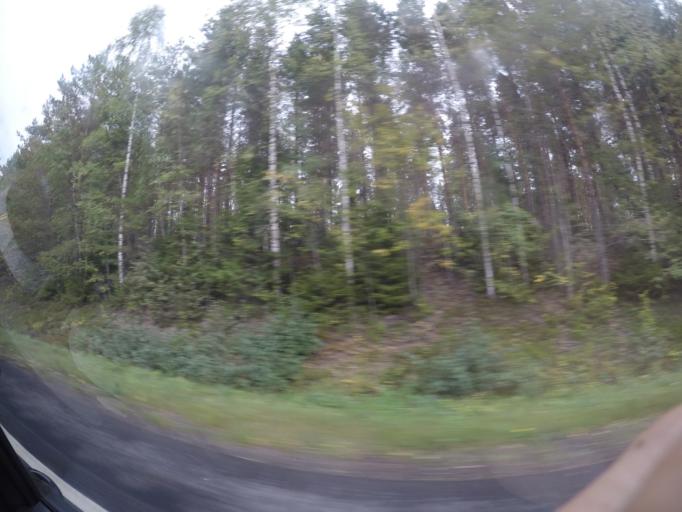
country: FI
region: Haeme
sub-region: Haemeenlinna
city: Parola
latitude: 61.1323
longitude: 24.4177
